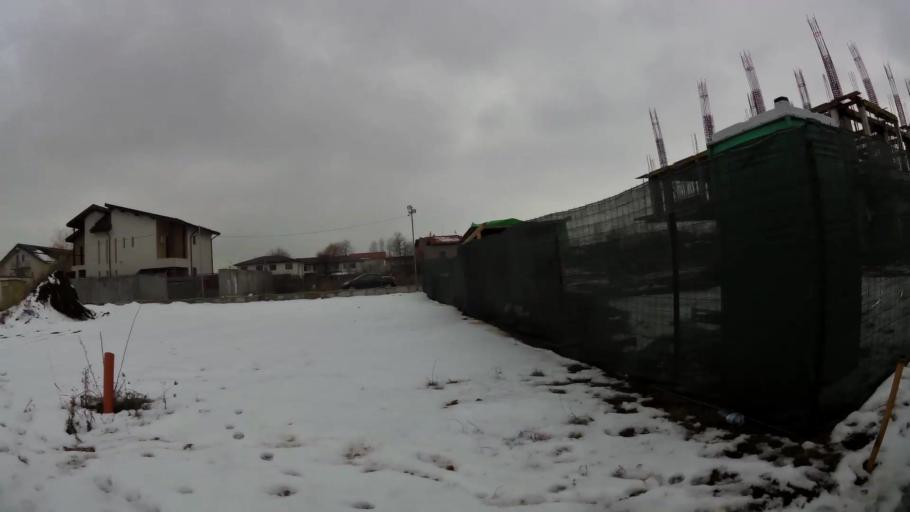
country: RO
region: Ilfov
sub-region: Comuna Otopeni
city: Otopeni
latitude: 44.5448
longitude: 26.0757
